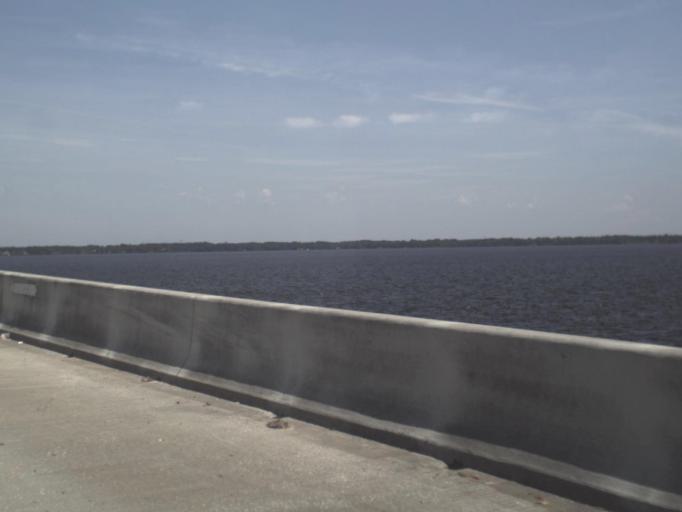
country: US
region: Florida
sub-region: Clay County
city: Orange Park
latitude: 30.1901
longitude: -81.6745
